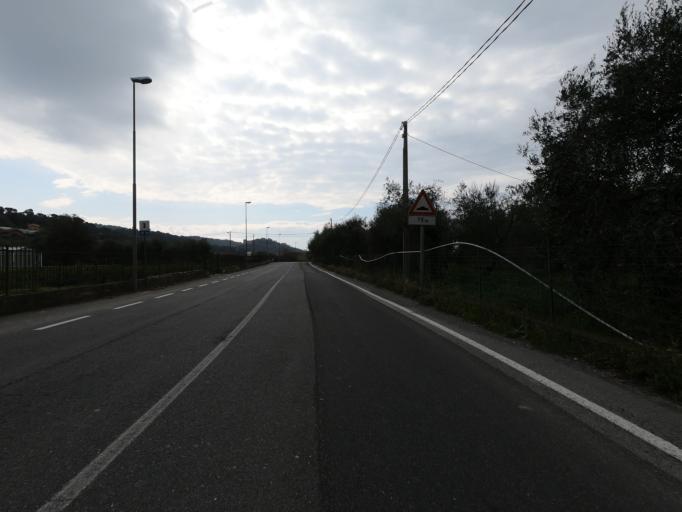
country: IT
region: Liguria
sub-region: Provincia di Savona
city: Andora
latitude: 43.9755
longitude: 8.1364
